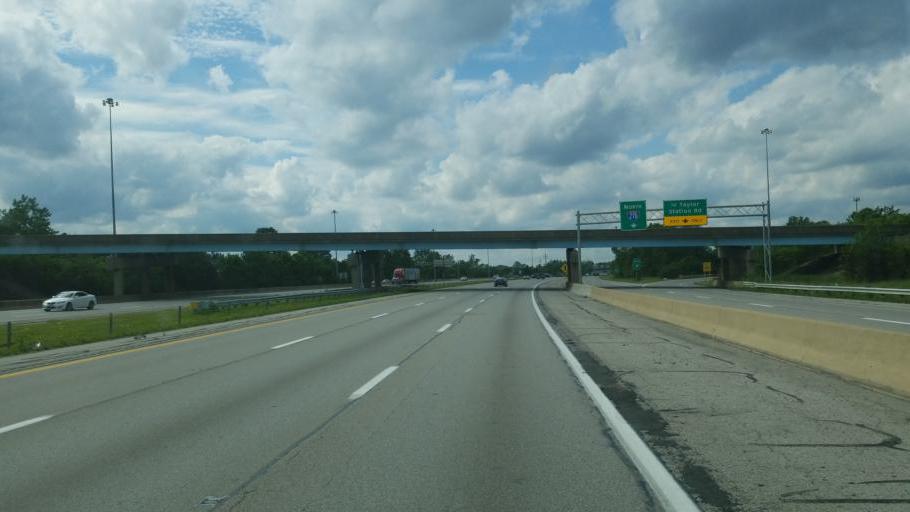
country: US
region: Ohio
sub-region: Franklin County
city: Whitehall
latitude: 39.9790
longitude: -82.8531
